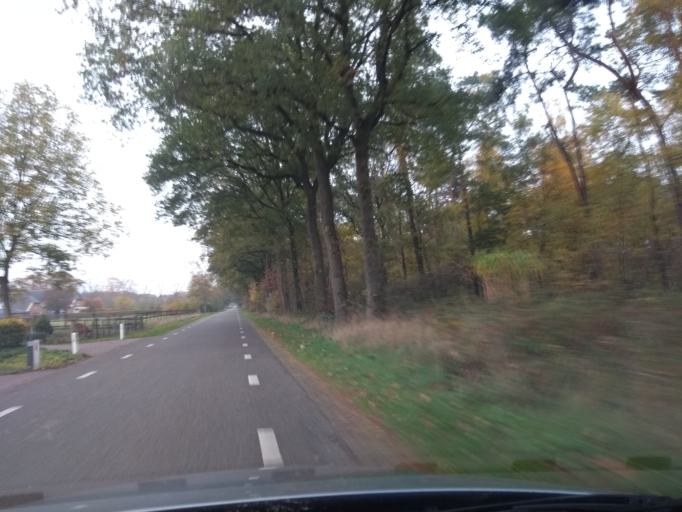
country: NL
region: Gelderland
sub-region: Gemeente Bronckhorst
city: Hengelo
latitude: 52.0381
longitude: 6.3369
